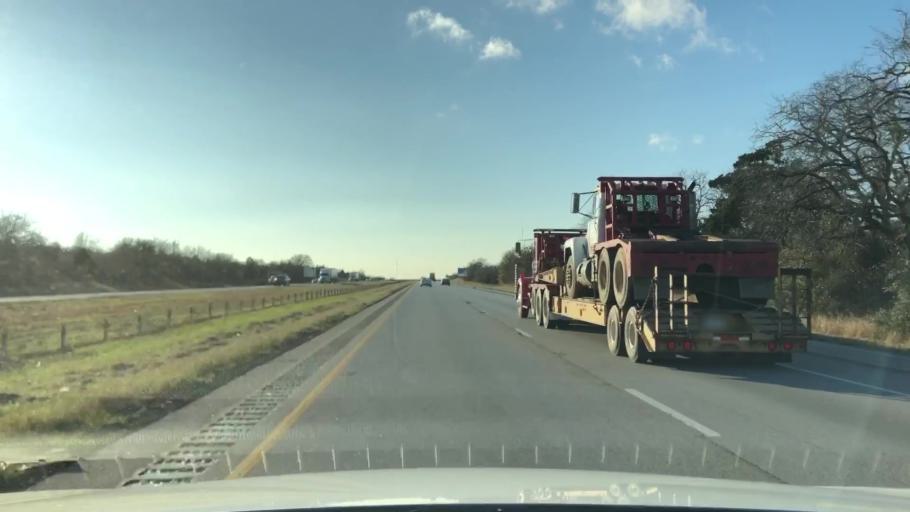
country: US
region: Texas
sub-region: Fayette County
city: Flatonia
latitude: 29.6966
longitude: -97.1168
